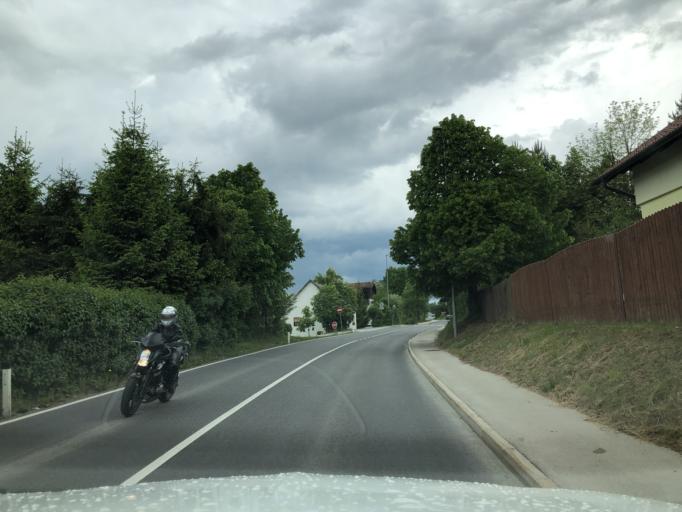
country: SI
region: Cerknica
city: Cerknica
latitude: 45.7953
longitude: 14.3421
